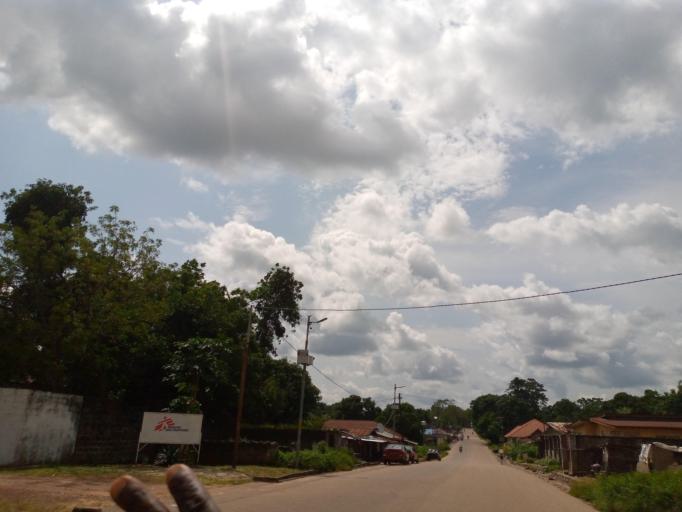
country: SL
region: Northern Province
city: Magburaka
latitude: 8.7158
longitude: -11.9370
